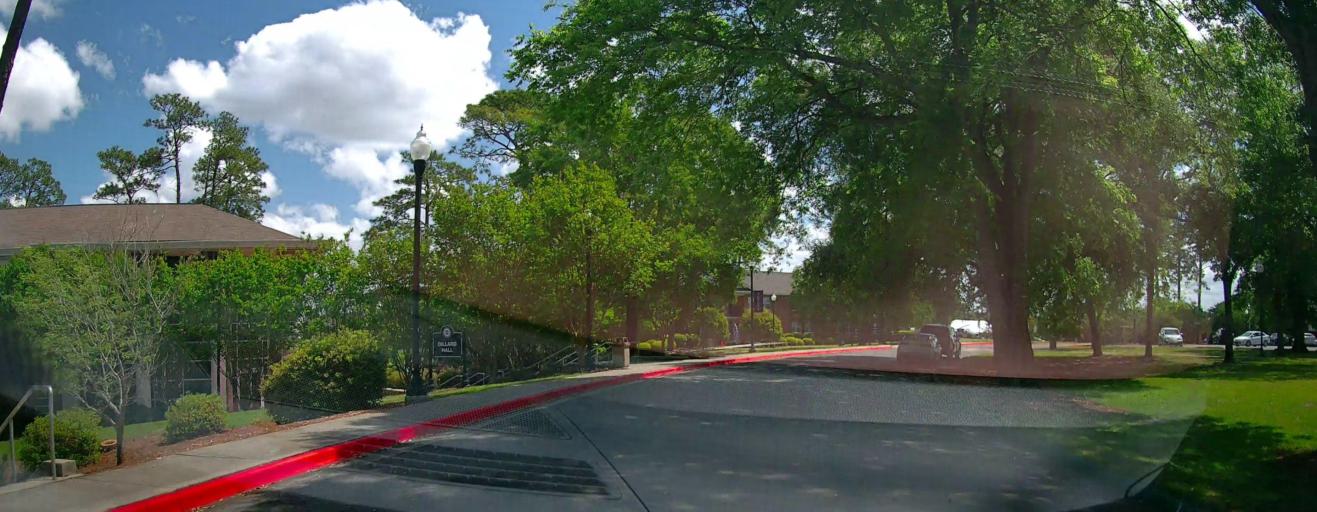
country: US
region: Georgia
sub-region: Bleckley County
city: Cochran
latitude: 32.3811
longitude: -83.3453
